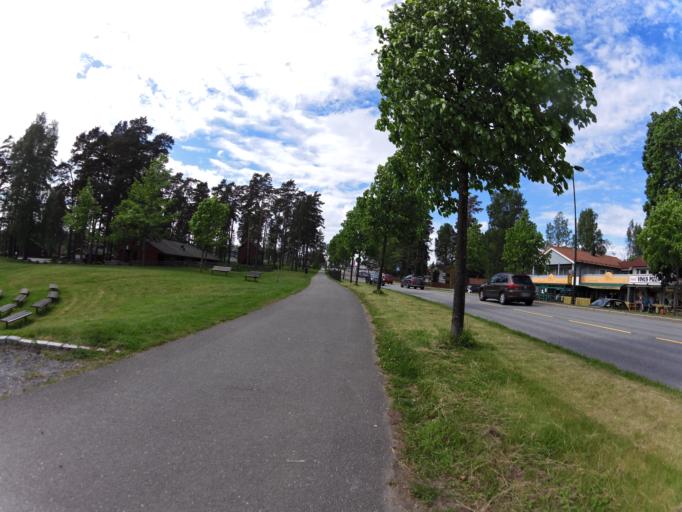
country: NO
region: Ostfold
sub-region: Rade
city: Karlshus
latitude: 59.3528
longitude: 10.8697
